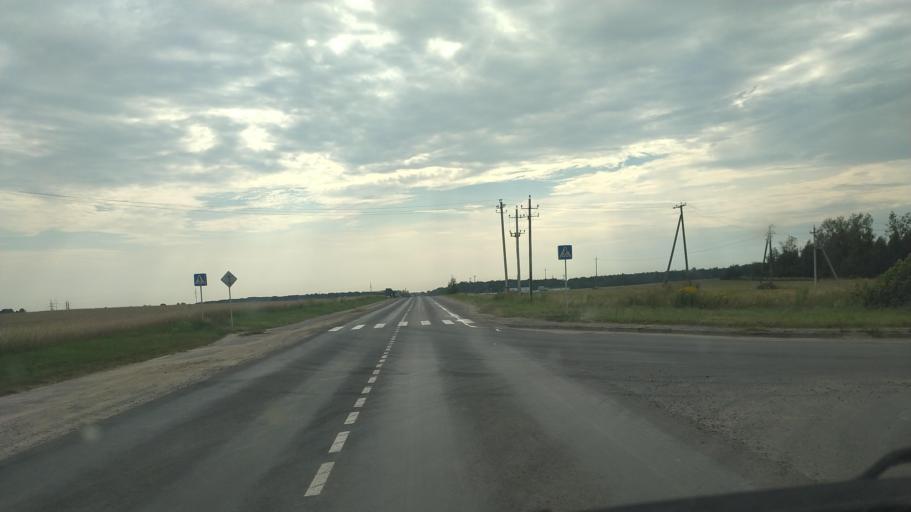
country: BY
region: Brest
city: Byaroza
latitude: 52.5507
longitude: 24.9392
